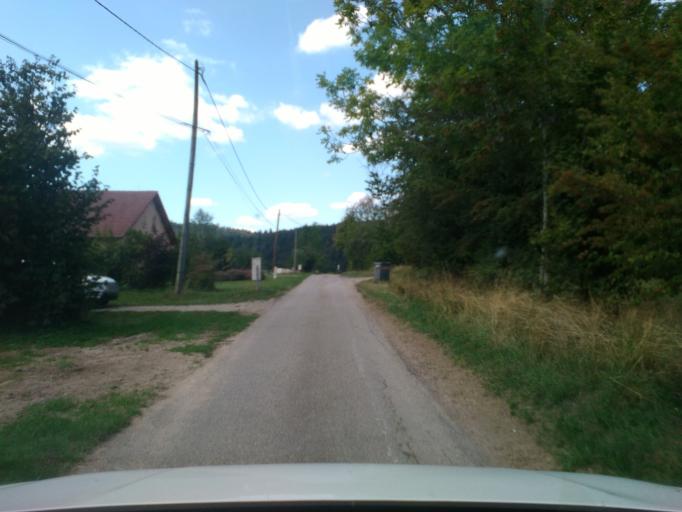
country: FR
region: Lorraine
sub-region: Departement des Vosges
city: Corcieux
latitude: 48.1445
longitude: 6.9113
